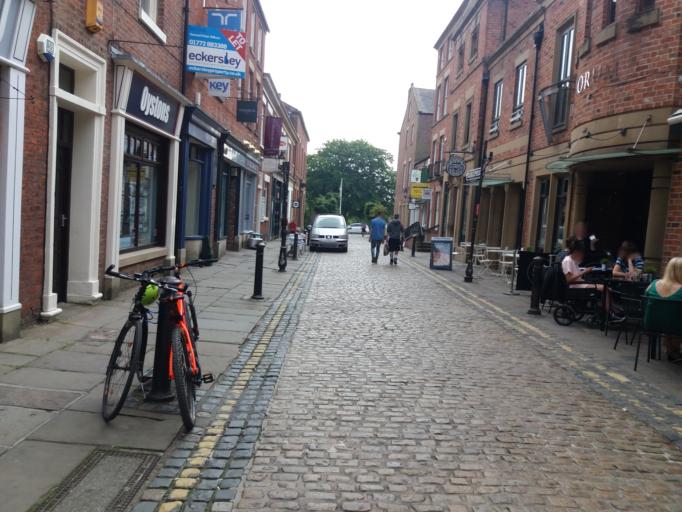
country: GB
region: England
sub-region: Lancashire
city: Preston
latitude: 53.7575
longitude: -2.7021
